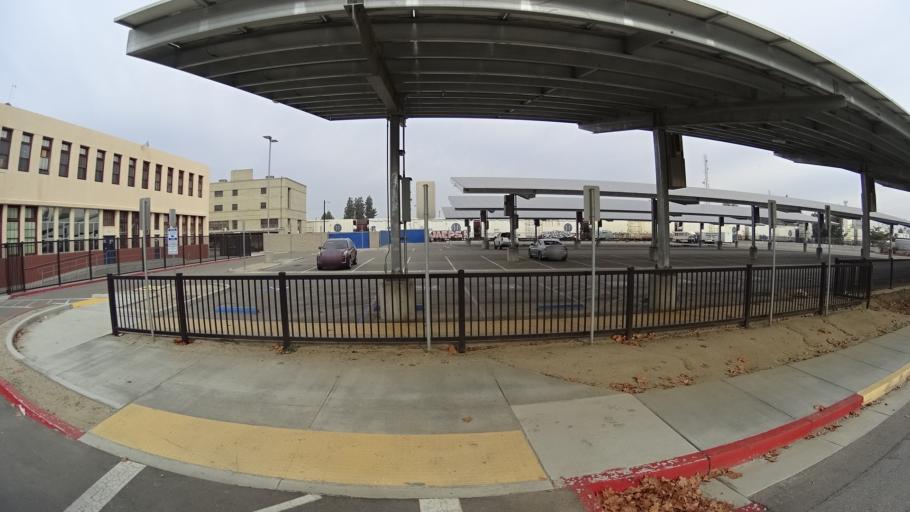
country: US
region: California
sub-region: Kern County
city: Bakersfield
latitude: 35.3704
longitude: -119.0223
